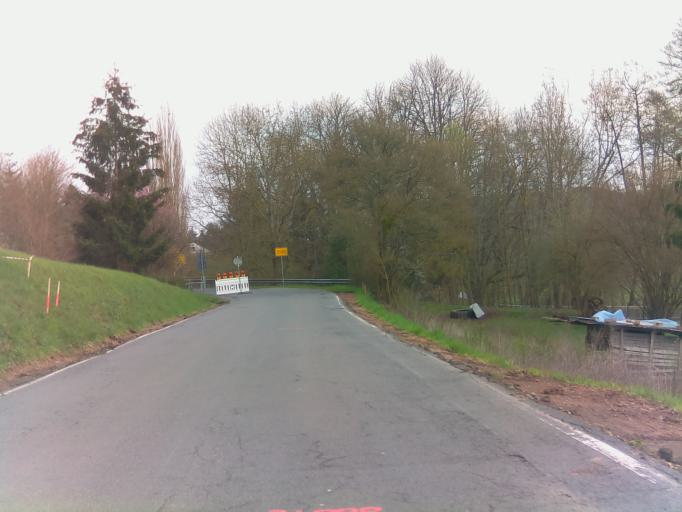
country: DE
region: Rheinland-Pfalz
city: Bockenau
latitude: 49.8378
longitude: 7.6717
